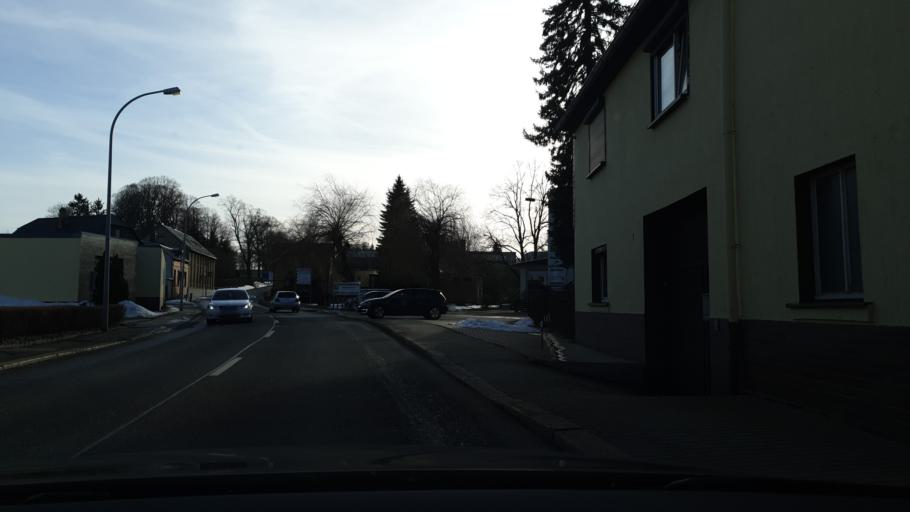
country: DE
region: Thuringia
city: Triebes
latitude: 50.6821
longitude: 12.0169
